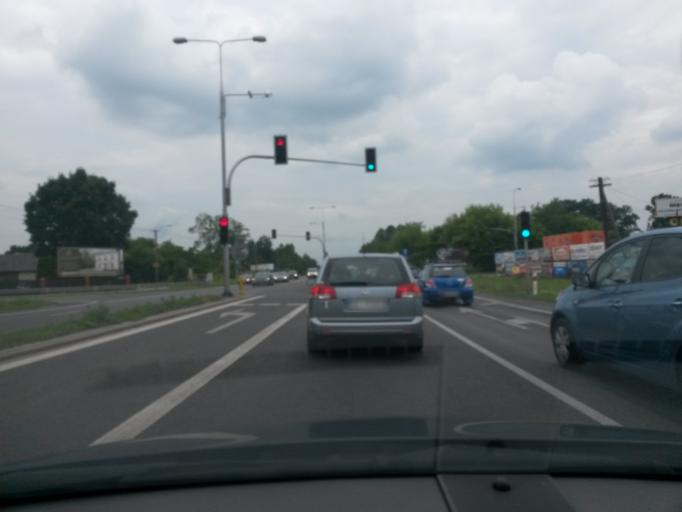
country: PL
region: Lodz Voivodeship
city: Zabia Wola
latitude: 52.0544
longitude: 20.7242
